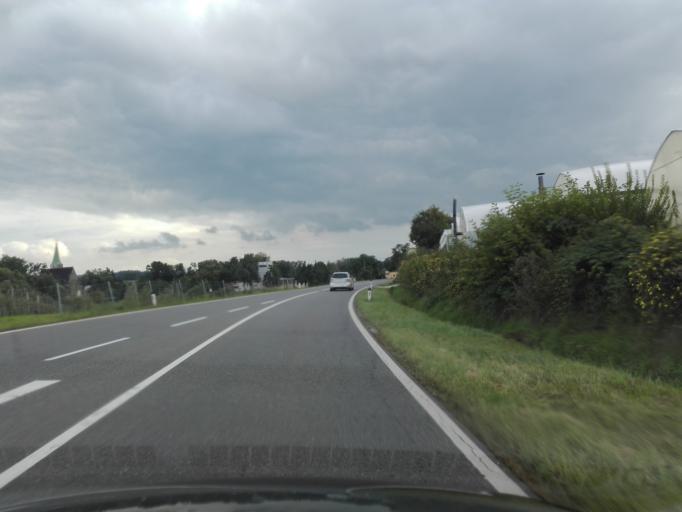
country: DE
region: Bavaria
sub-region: Lower Bavaria
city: Bad Fussing
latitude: 48.2967
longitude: 13.3319
